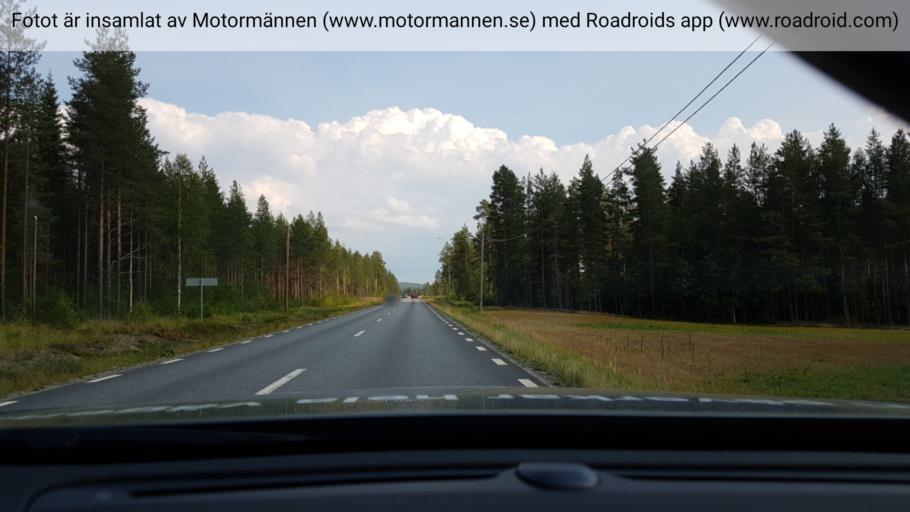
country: SE
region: Vaesterbotten
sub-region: Bjurholms Kommun
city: Bjurholm
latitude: 64.2880
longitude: 19.2003
